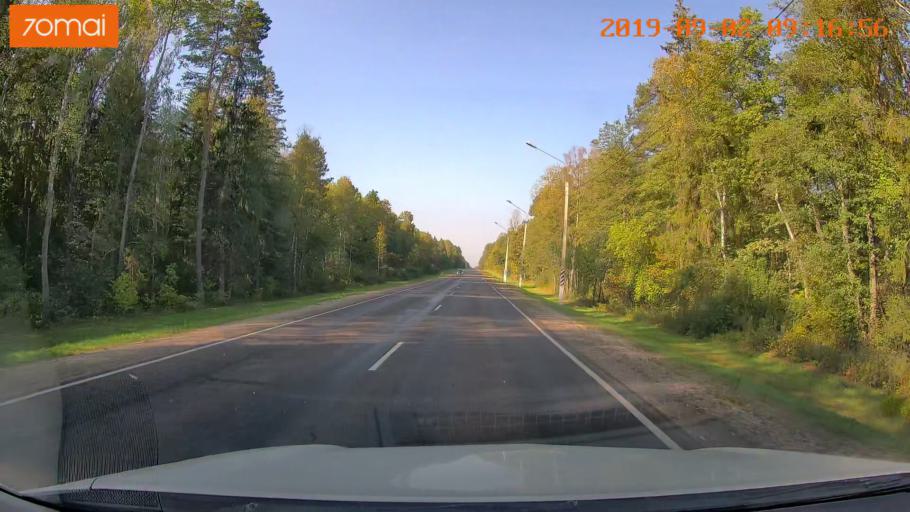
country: RU
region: Kaluga
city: Nikola-Lenivets
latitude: 54.8286
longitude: 35.4641
